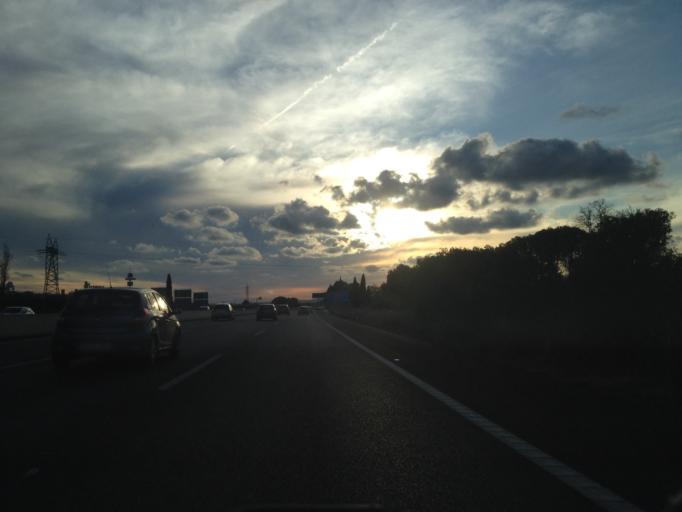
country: ES
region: Balearic Islands
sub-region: Illes Balears
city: Marratxi
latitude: 39.6197
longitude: 2.7069
